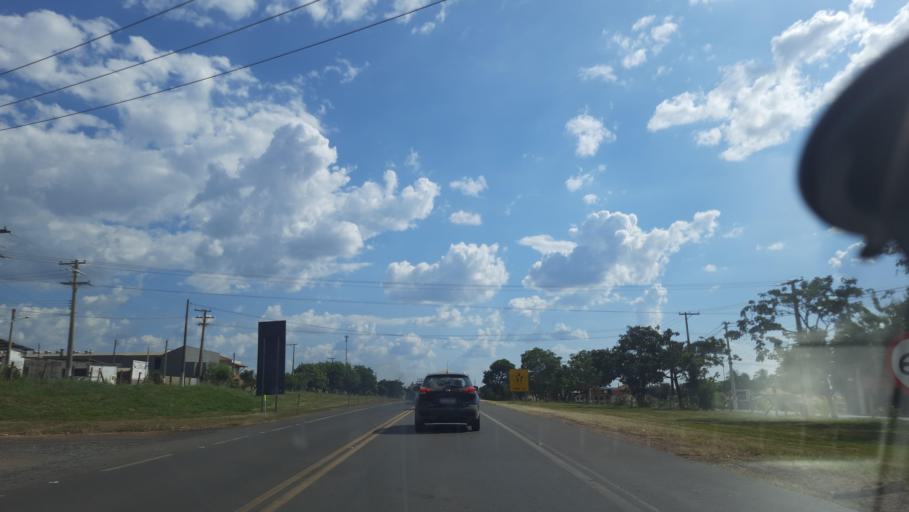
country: BR
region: Sao Paulo
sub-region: Vargem Grande Do Sul
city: Vargem Grande do Sul
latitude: -21.7323
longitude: -46.9686
